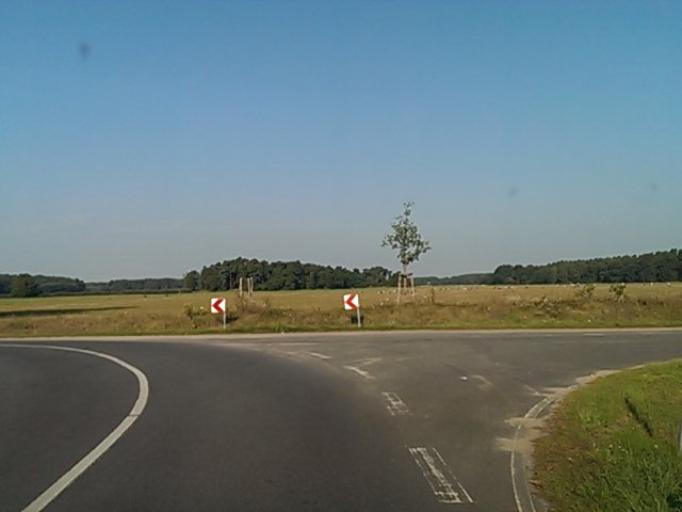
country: DE
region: Brandenburg
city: Trebbin
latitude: 52.1915
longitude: 13.1320
